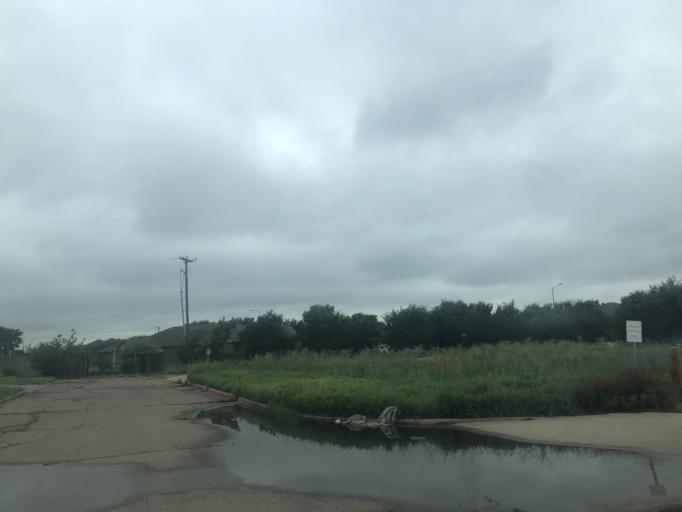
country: US
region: Texas
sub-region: Dallas County
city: Cockrell Hill
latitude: 32.7796
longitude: -96.8640
